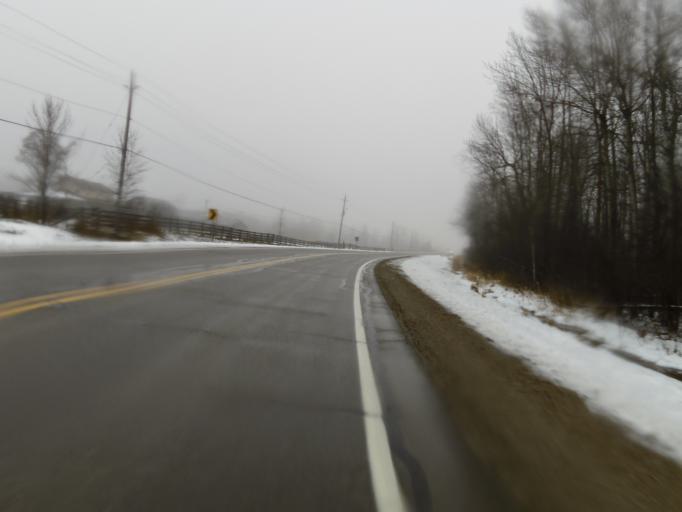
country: CA
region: Ontario
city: Perth
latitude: 44.8288
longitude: -76.3913
